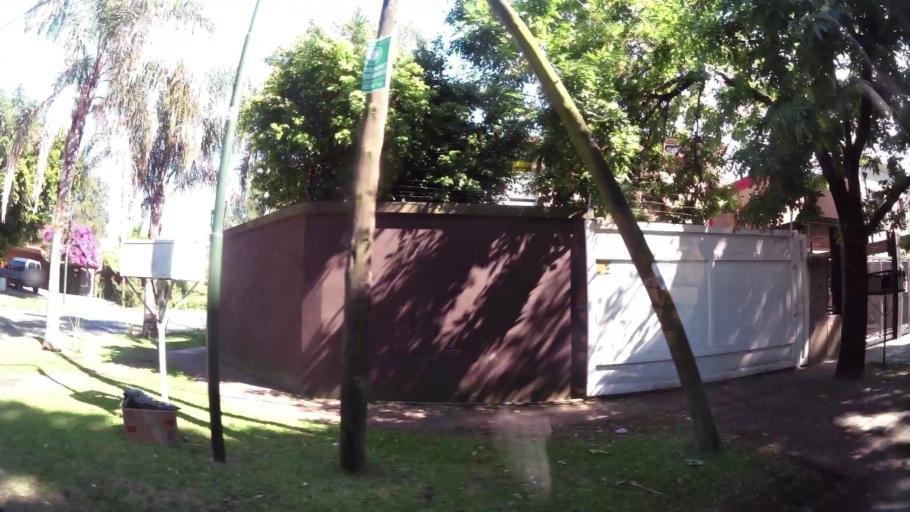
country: AR
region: Buenos Aires
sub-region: Partido de Tigre
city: Tigre
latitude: -34.4827
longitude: -58.5664
